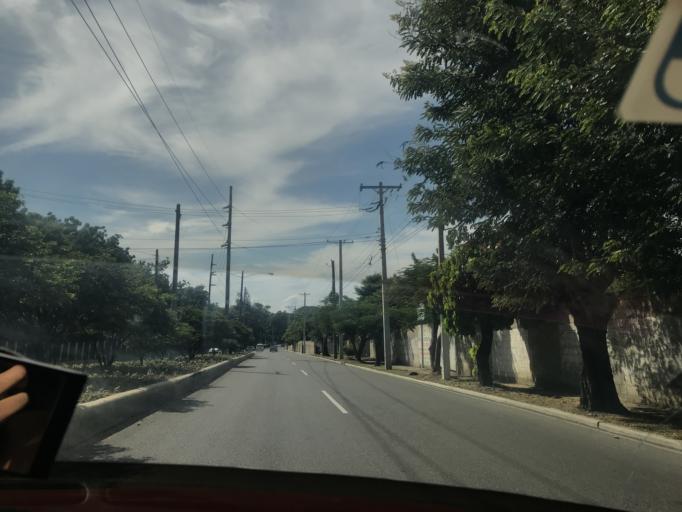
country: DO
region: Santiago
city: Santiago de los Caballeros
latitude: 19.4495
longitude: -70.7438
